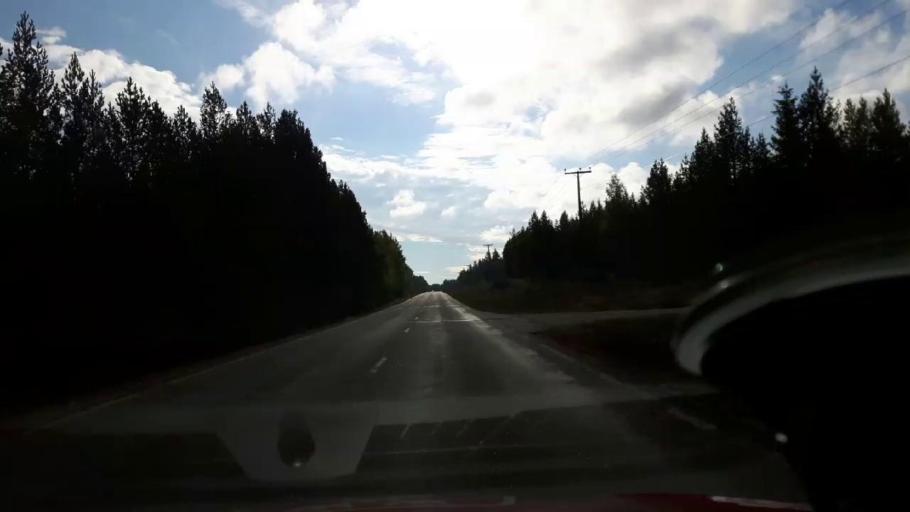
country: SE
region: Jaemtland
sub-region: Harjedalens Kommun
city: Sveg
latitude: 62.0977
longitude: 15.0785
